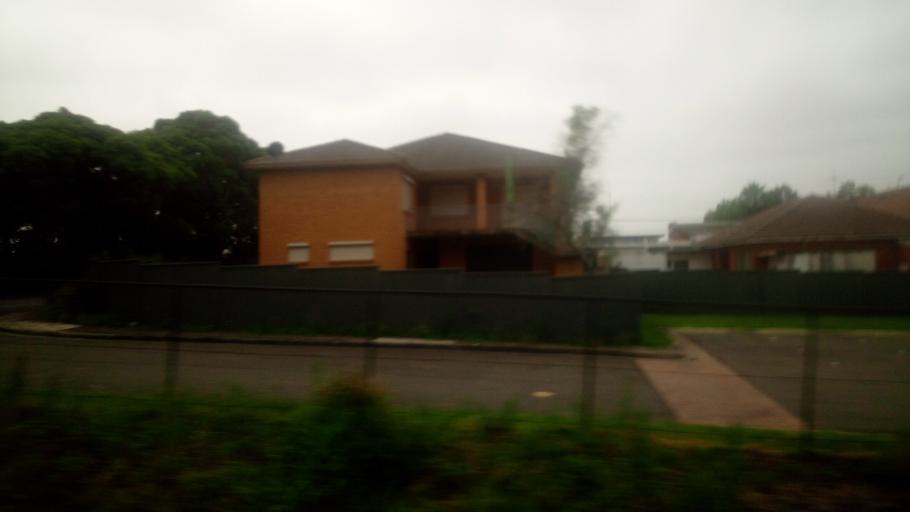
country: AU
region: New South Wales
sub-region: Blue Mountains Municipality
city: Blaxland
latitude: -33.6940
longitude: 150.5469
